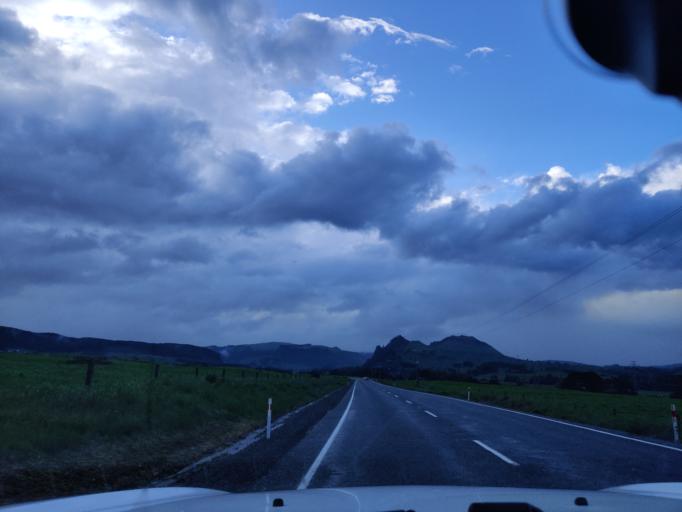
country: NZ
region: Waikato
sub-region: South Waikato District
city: Tokoroa
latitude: -38.4034
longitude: 175.7908
